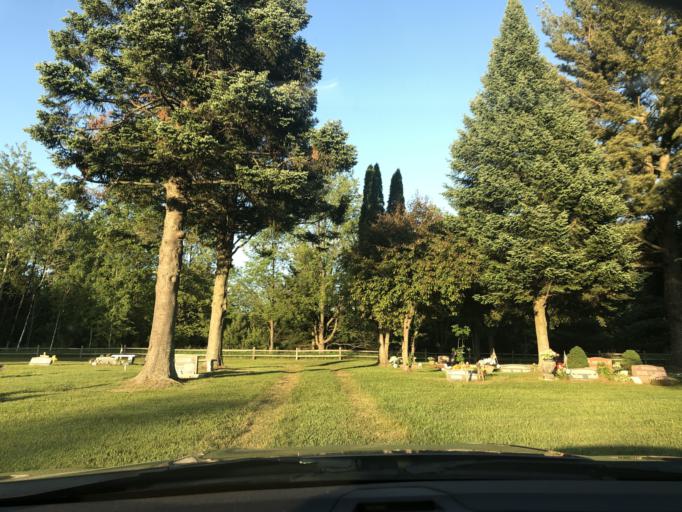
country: US
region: Michigan
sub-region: Missaukee County
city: Lake City
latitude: 44.4676
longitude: -85.1242
